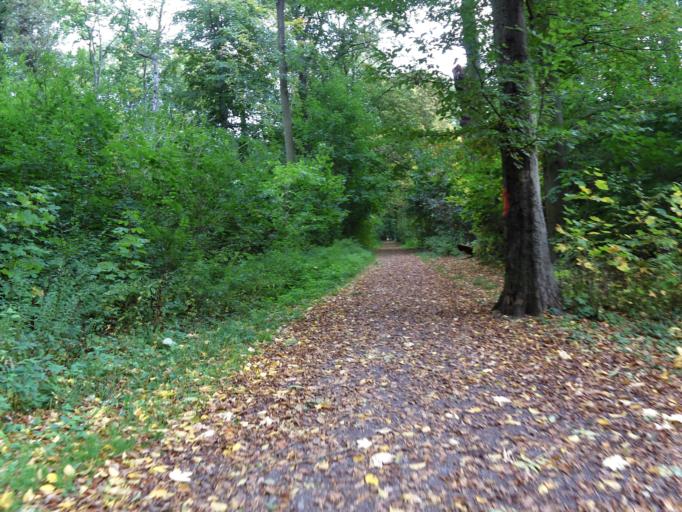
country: DE
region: Saxony
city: Leipzig
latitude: 51.3152
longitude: 12.3532
